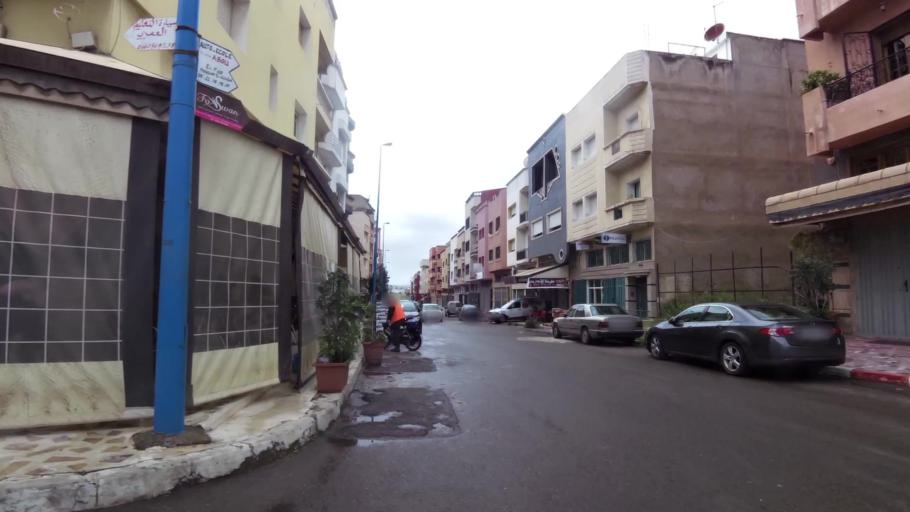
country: MA
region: Grand Casablanca
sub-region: Casablanca
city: Casablanca
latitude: 33.5349
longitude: -7.6485
